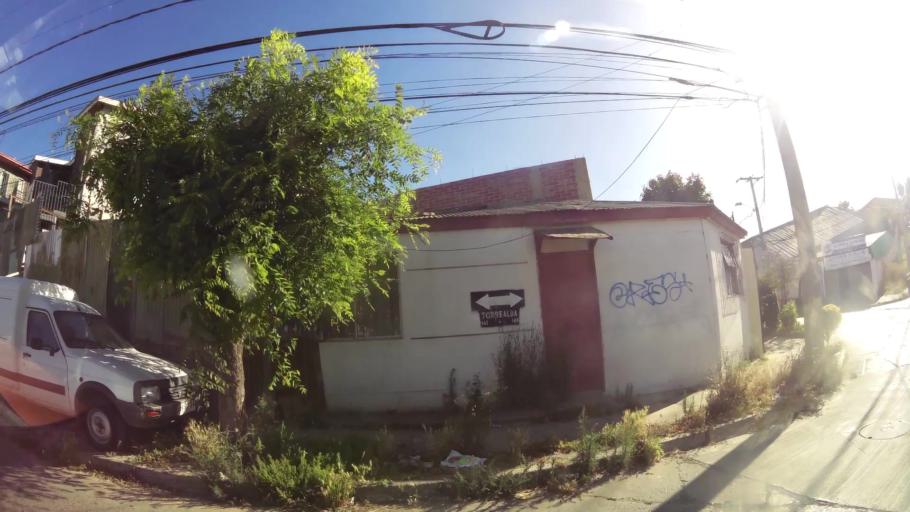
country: CL
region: Valparaiso
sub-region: Provincia de Valparaiso
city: Vina del Mar
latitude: -33.0313
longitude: -71.5668
